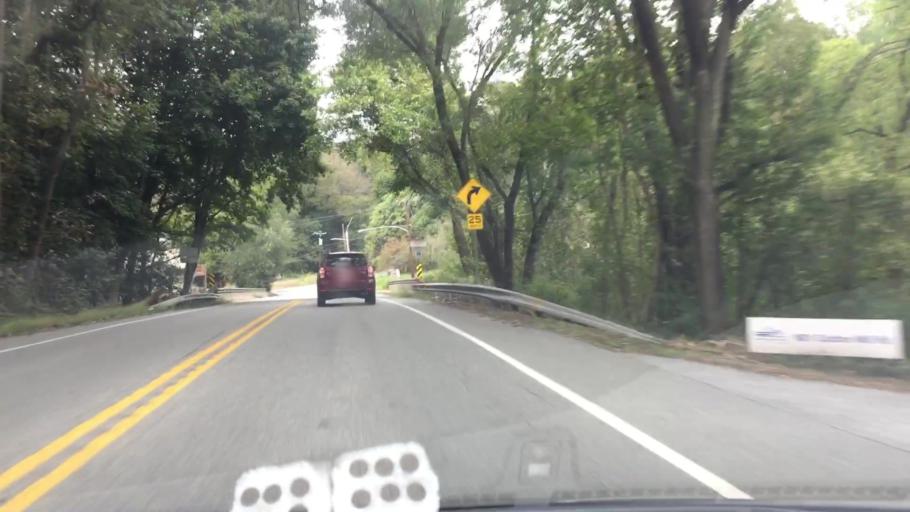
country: US
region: Pennsylvania
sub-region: Delaware County
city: Village Green-Green Ridge
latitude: 39.8686
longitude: -75.4087
